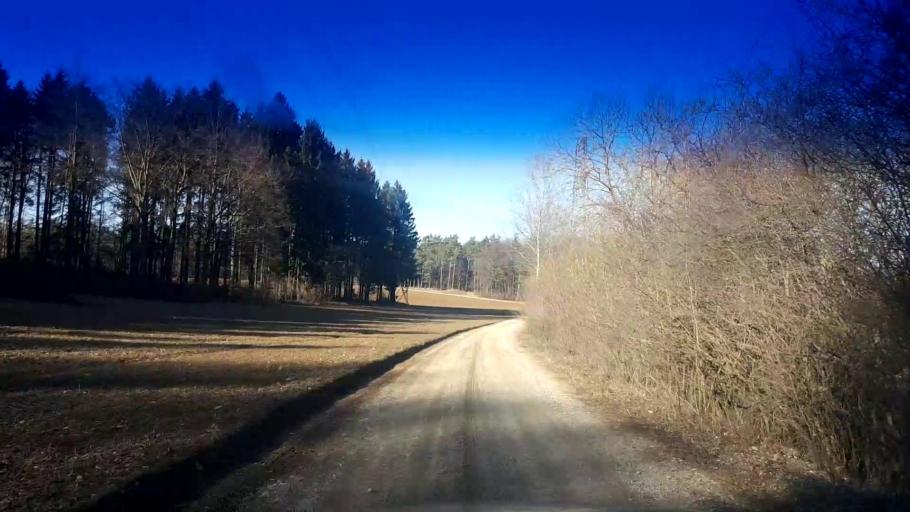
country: DE
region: Bavaria
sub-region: Upper Franconia
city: Poxdorf
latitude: 49.9645
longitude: 11.0858
